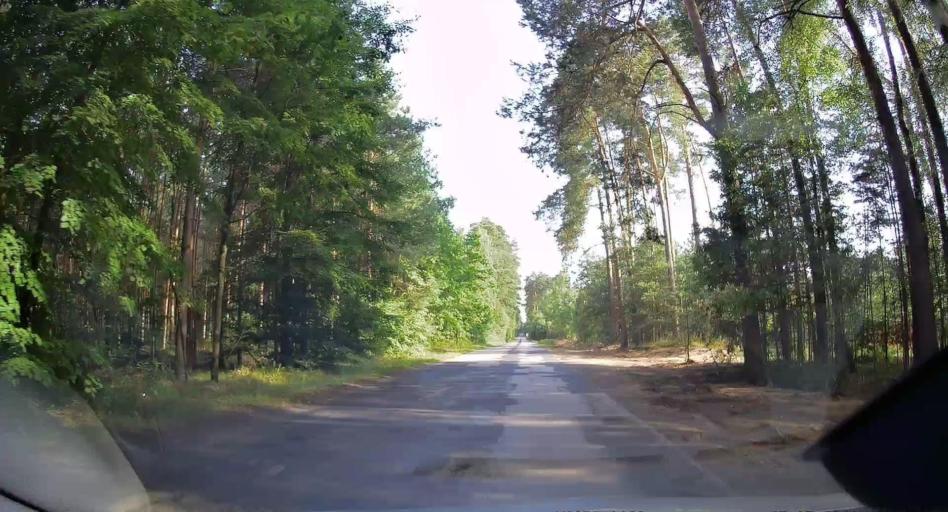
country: PL
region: Swietokrzyskie
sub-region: Powiat konecki
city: Konskie
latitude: 51.2359
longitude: 20.3815
